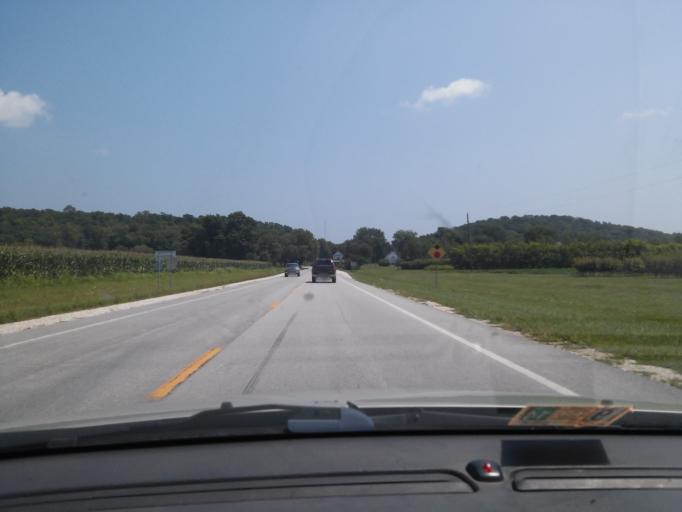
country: US
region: Missouri
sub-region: Pike County
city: Louisiana
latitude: 39.5114
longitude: -90.9732
